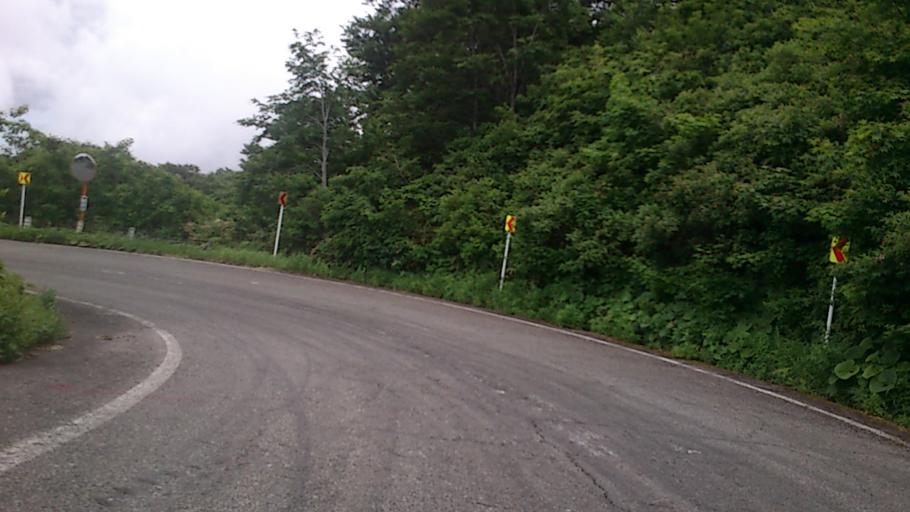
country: JP
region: Yamagata
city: Yuza
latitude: 39.1068
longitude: 139.9686
